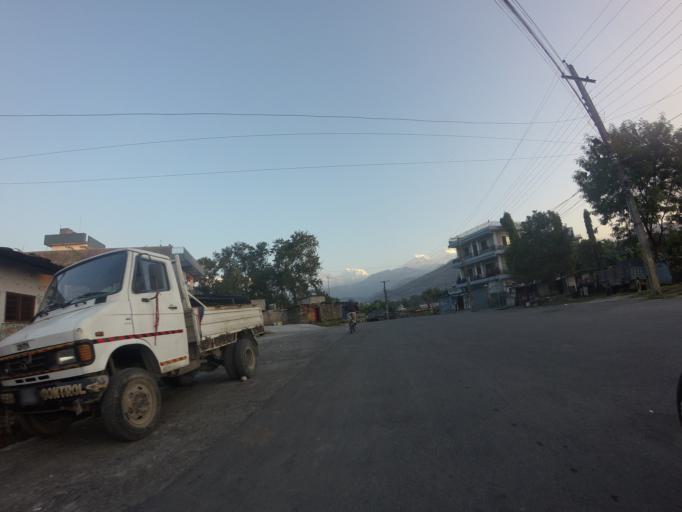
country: NP
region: Western Region
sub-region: Gandaki Zone
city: Pokhara
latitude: 28.2093
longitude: 83.9944
